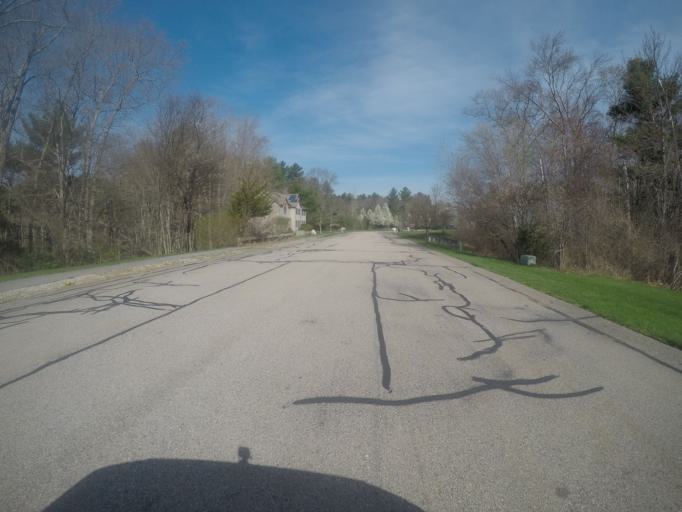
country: US
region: Massachusetts
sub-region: Bristol County
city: Easton
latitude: 42.0134
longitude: -71.1172
